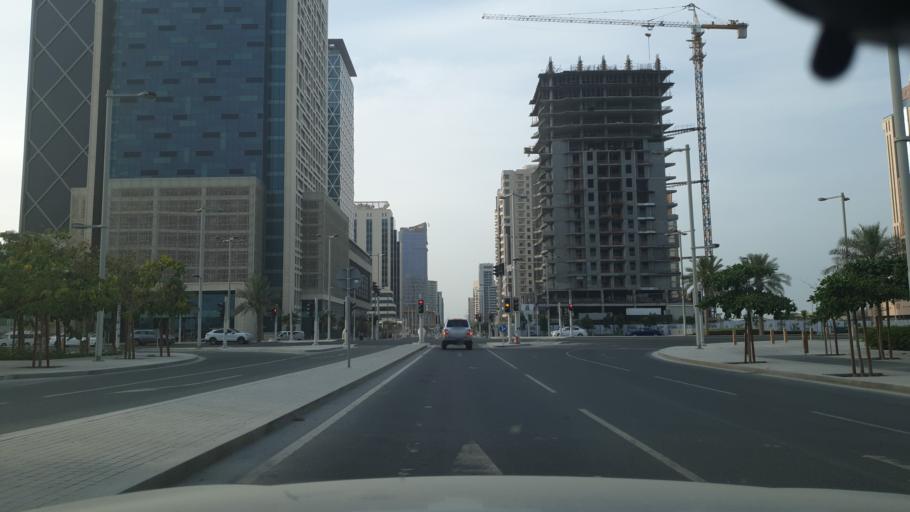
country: QA
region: Baladiyat ad Dawhah
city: Doha
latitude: 25.3825
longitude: 51.5262
